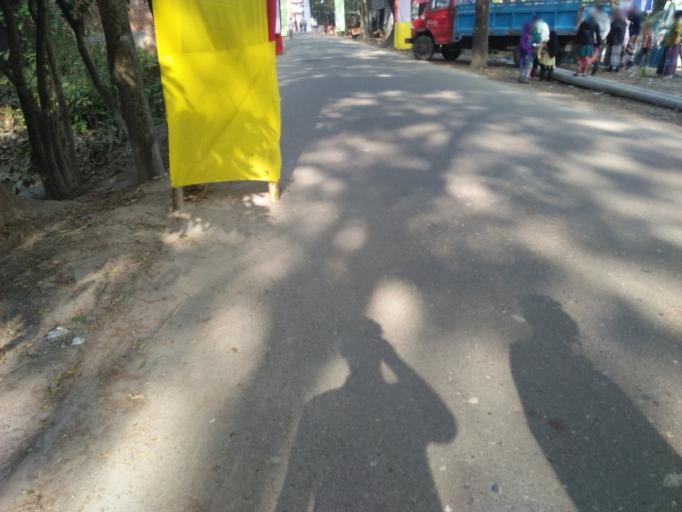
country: BD
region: Khulna
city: Uttar Char Fasson
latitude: 22.1904
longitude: 90.6763
